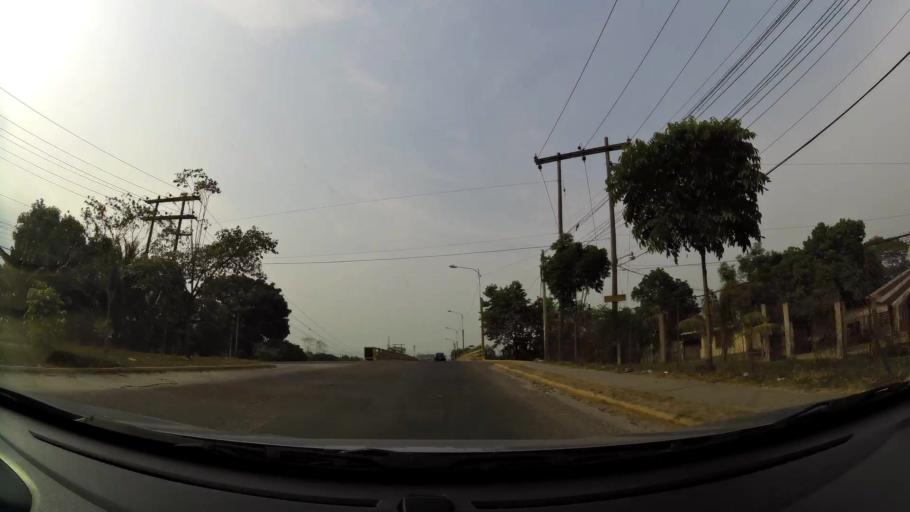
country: HN
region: Cortes
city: San Pedro Sula
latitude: 15.5311
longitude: -88.0143
